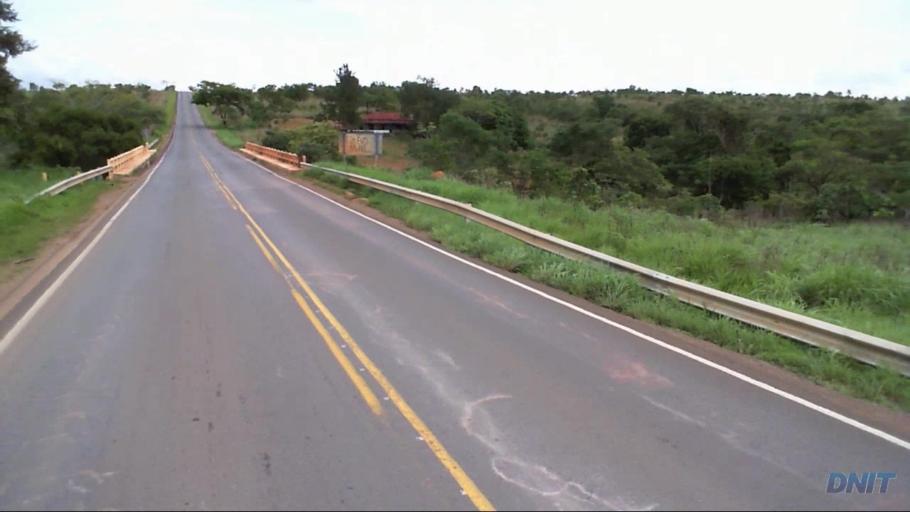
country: BR
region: Goias
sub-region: Padre Bernardo
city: Padre Bernardo
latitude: -15.2965
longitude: -48.2381
